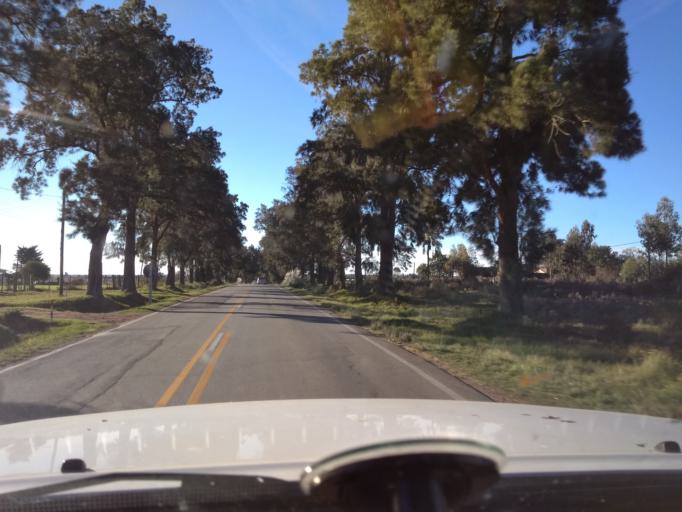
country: UY
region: Canelones
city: San Bautista
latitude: -34.3968
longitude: -55.9596
